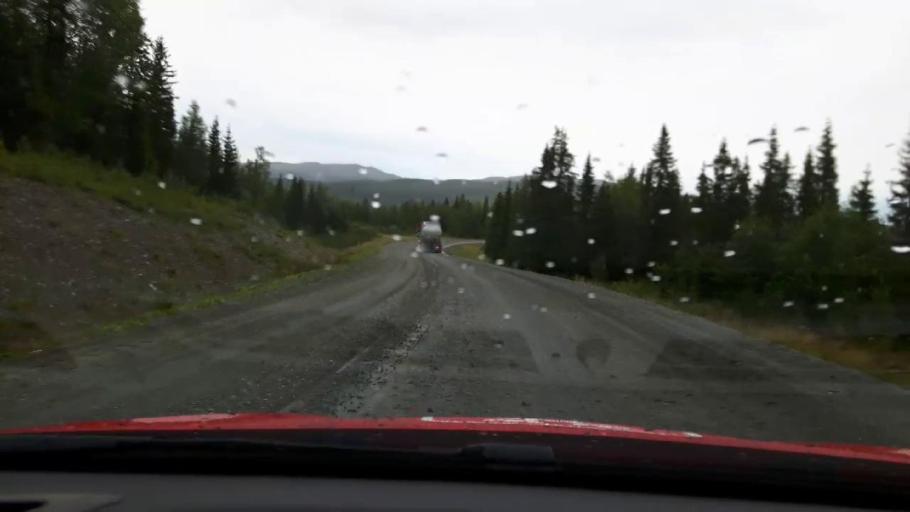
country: SE
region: Jaemtland
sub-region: Are Kommun
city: Are
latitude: 63.4112
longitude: 12.7760
